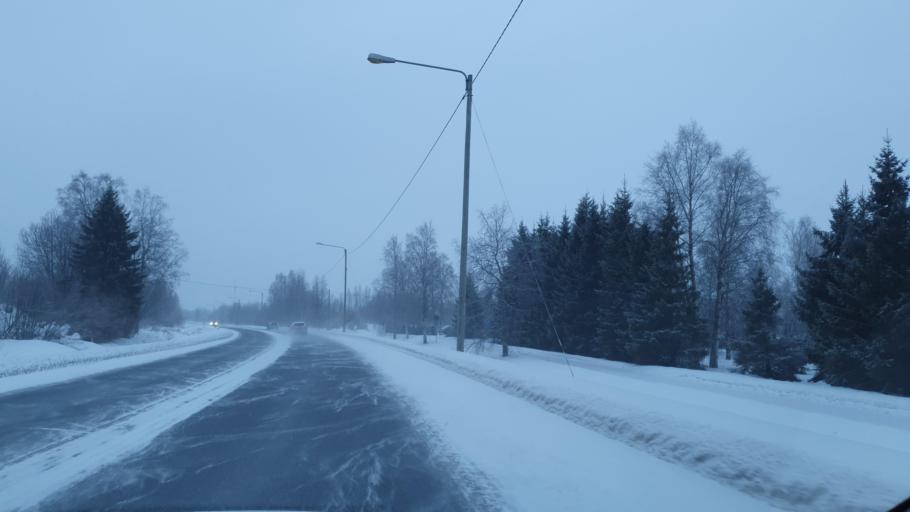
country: FI
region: Lapland
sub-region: Kemi-Tornio
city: Tornio
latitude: 65.8792
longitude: 24.1546
